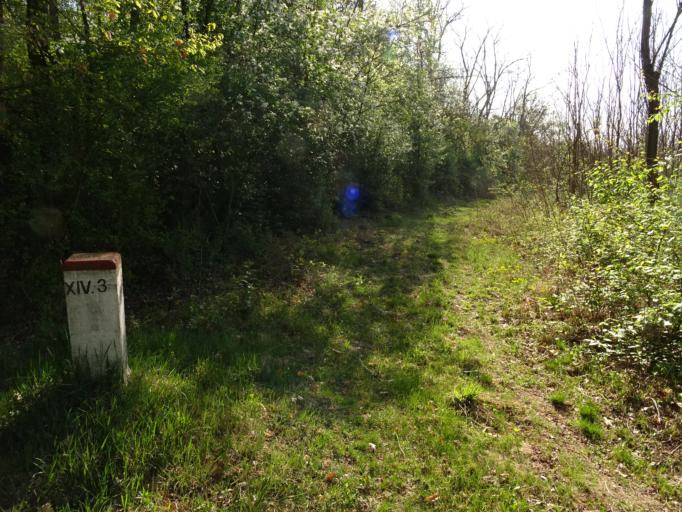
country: SK
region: Kosicky
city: Moldava nad Bodvou
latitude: 48.5323
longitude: 21.0151
